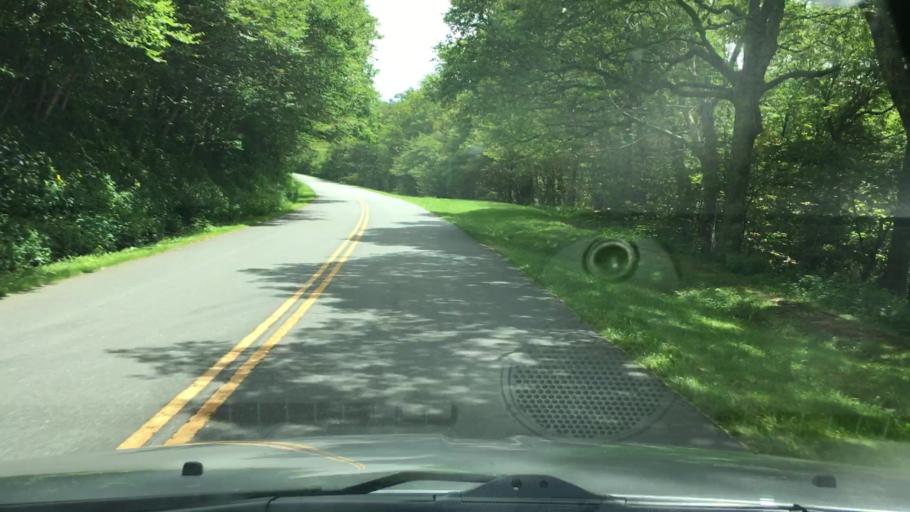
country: US
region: North Carolina
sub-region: Buncombe County
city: Swannanoa
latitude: 35.6859
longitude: -82.3896
